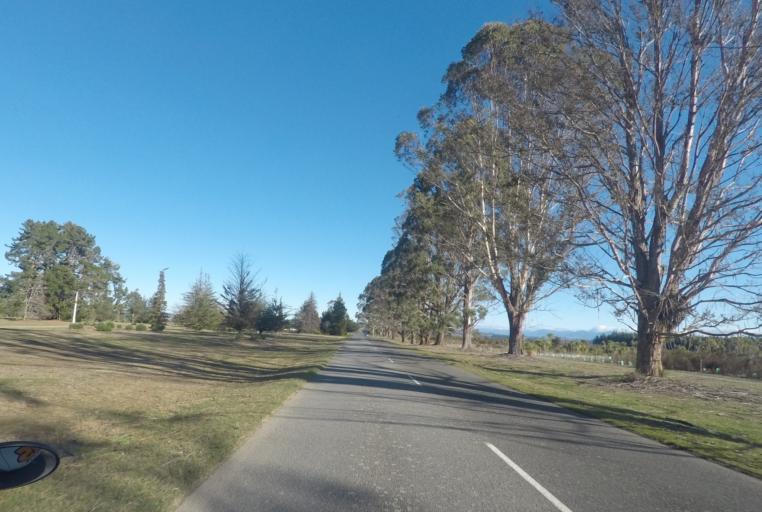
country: NZ
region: Tasman
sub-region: Tasman District
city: Mapua
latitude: -41.2810
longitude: 173.1375
